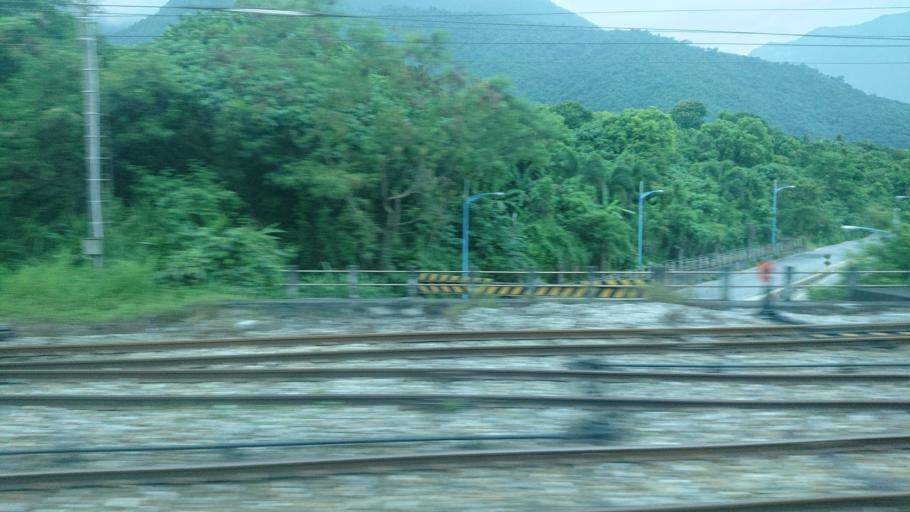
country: TW
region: Taiwan
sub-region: Hualien
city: Hualian
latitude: 24.1253
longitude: 121.6392
